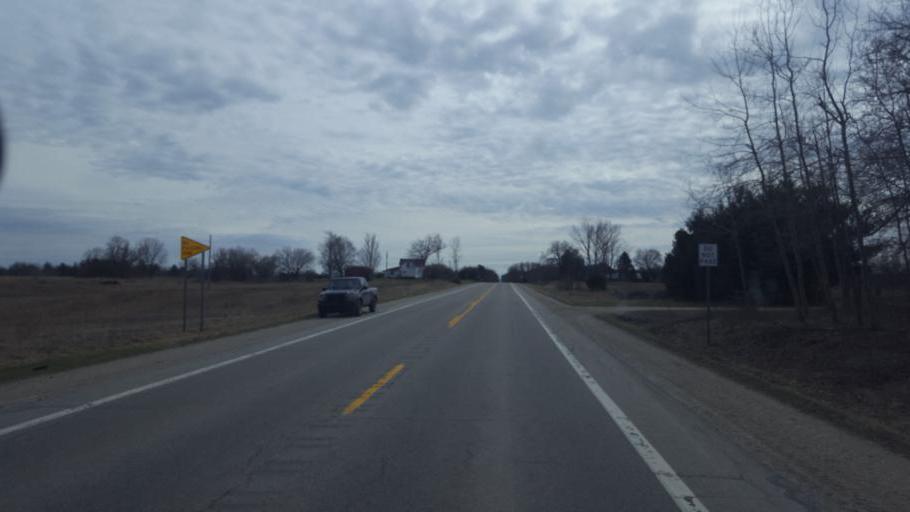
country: US
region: Michigan
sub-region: Isabella County
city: Lake Isabella
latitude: 43.7025
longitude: -85.1467
